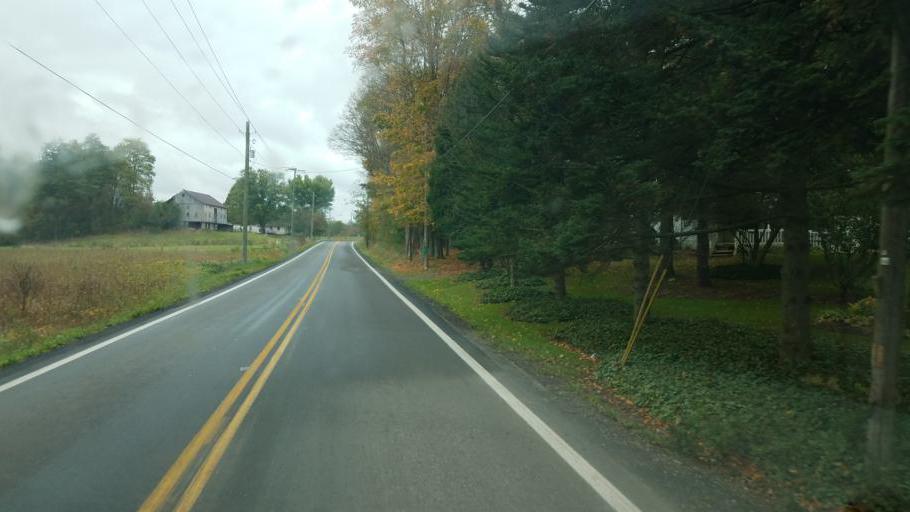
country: US
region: Ohio
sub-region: Holmes County
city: Millersburg
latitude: 40.6047
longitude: -81.8441
